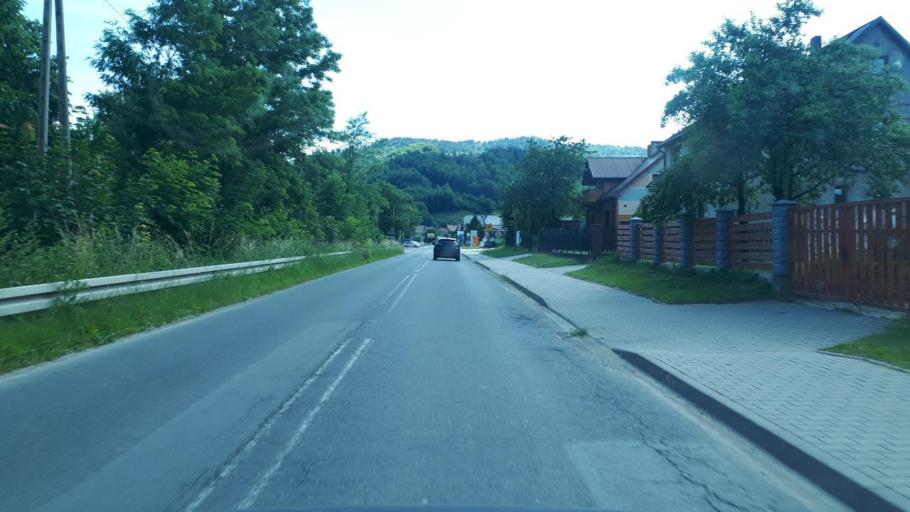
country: PL
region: Silesian Voivodeship
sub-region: Powiat zywiecki
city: Czernichow
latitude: 49.7543
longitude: 19.2102
